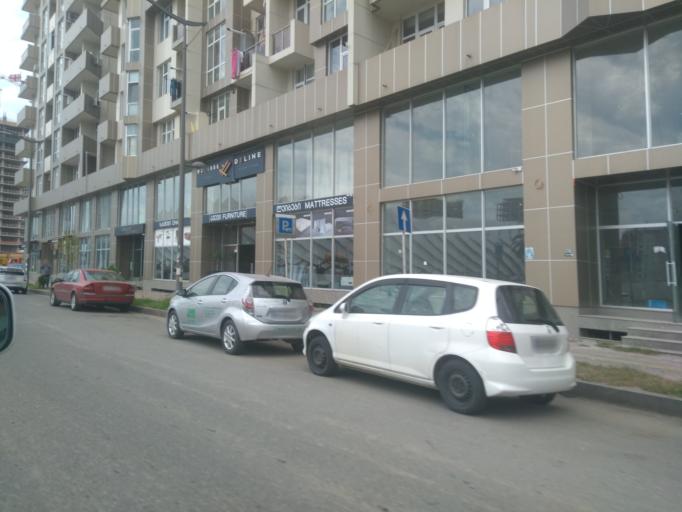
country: GE
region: Ajaria
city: Batumi
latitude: 41.6348
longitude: 41.6221
